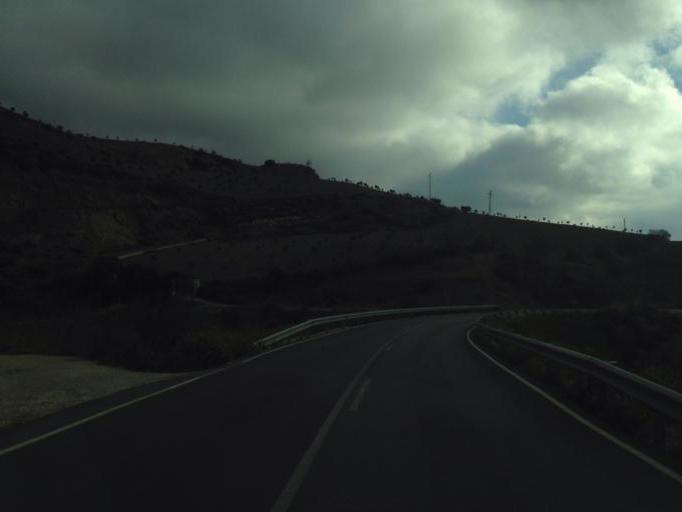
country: ES
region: Andalusia
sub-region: Provincia de Malaga
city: Casabermeja
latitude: 36.9356
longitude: -4.3906
